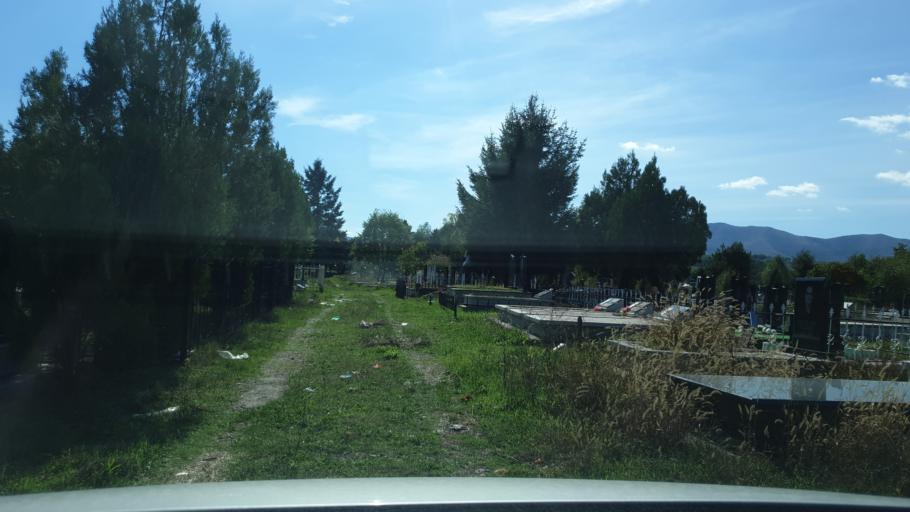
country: XK
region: Gjakova
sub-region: Komuna e Gjakoves
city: Gjakove
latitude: 42.3720
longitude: 20.4080
